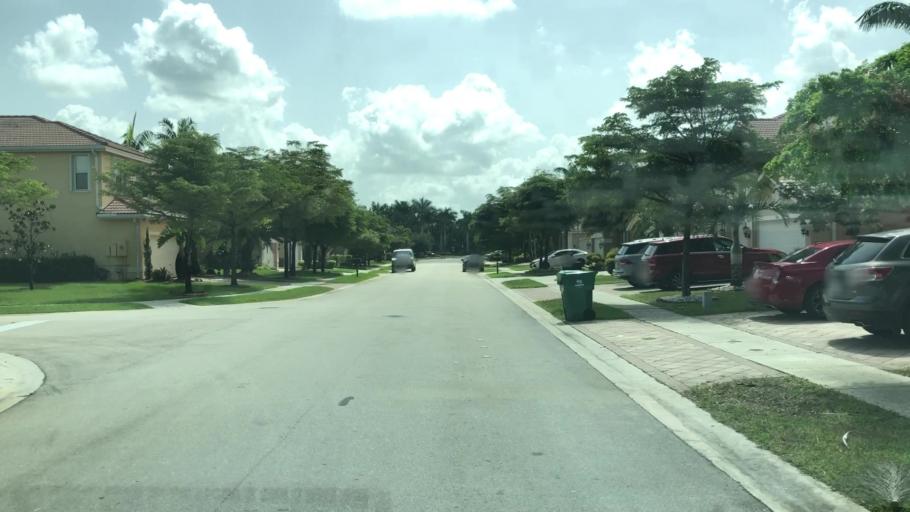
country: US
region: Florida
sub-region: Miami-Dade County
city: Palm Springs North
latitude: 25.9646
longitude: -80.3785
